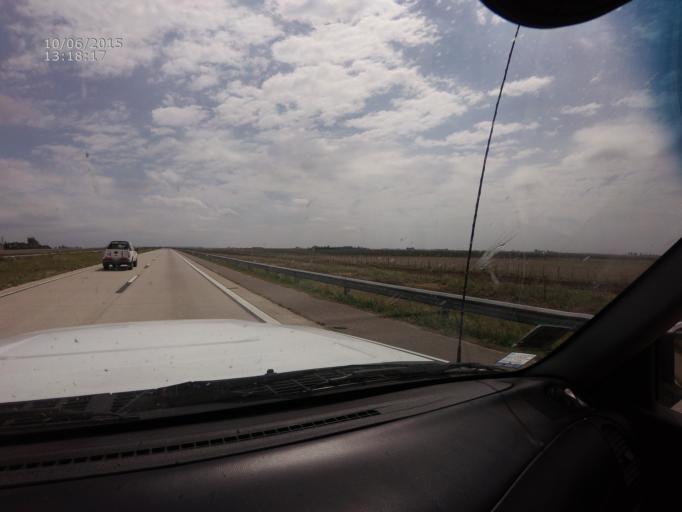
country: AR
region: Cordoba
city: Marcos Juarez
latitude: -32.6837
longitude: -62.0100
